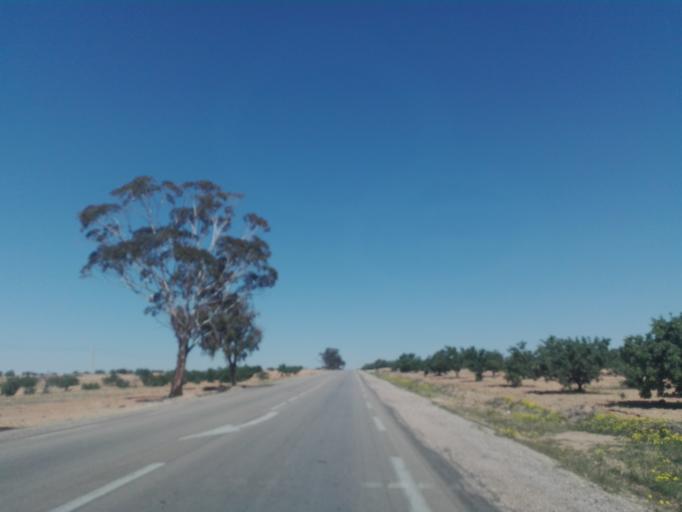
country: TN
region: Safaqis
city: Bi'r `Ali Bin Khalifah
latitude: 34.7478
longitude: 10.3535
